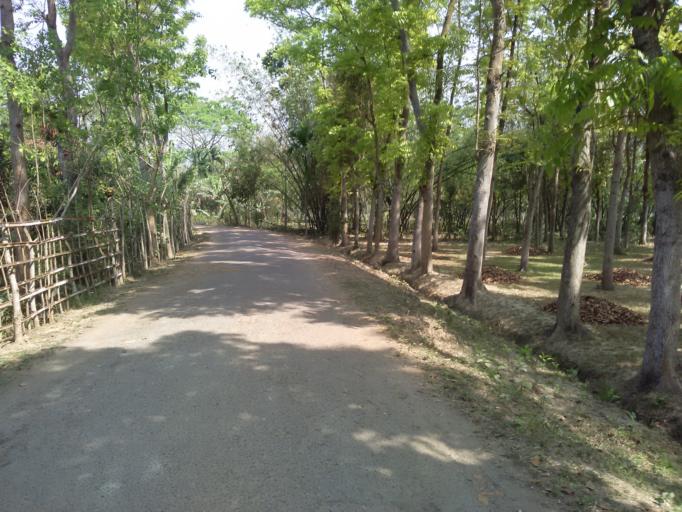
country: BD
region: Khulna
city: Khulna
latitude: 22.8814
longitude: 89.5395
